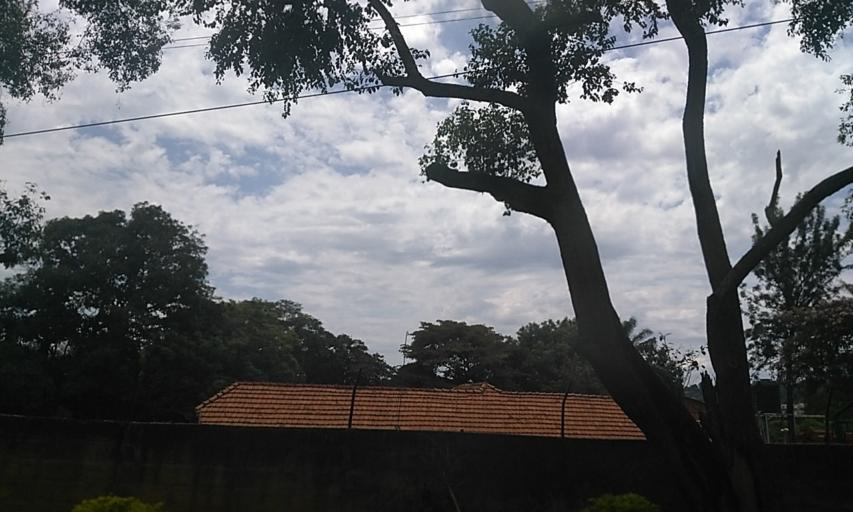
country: UG
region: Central Region
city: Kampala Central Division
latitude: 0.3374
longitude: 32.5850
